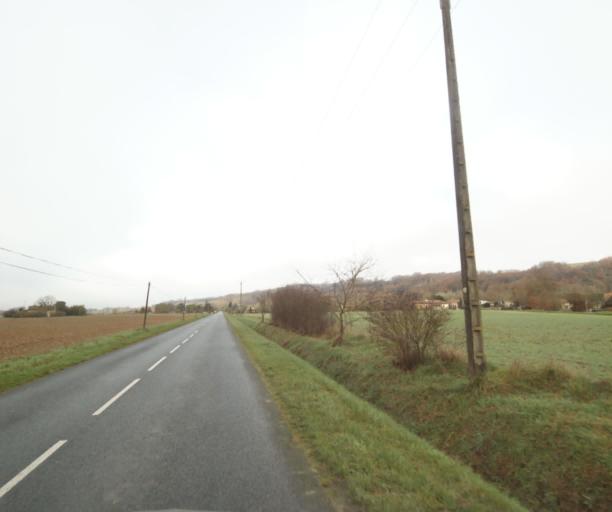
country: FR
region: Midi-Pyrenees
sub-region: Departement de la Haute-Garonne
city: Villemur-sur-Tarn
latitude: 43.8882
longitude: 1.4761
